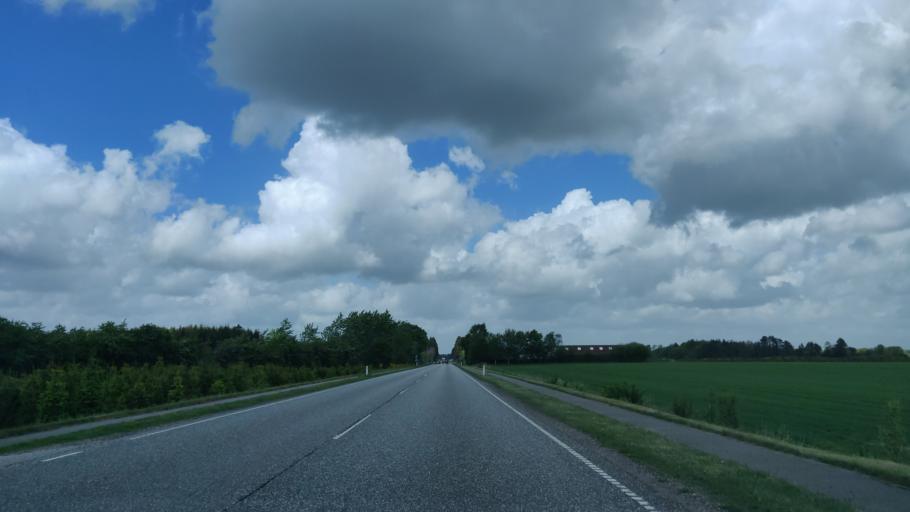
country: DK
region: Central Jutland
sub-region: Ikast-Brande Kommune
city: Bording Kirkeby
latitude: 56.2437
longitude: 9.3221
